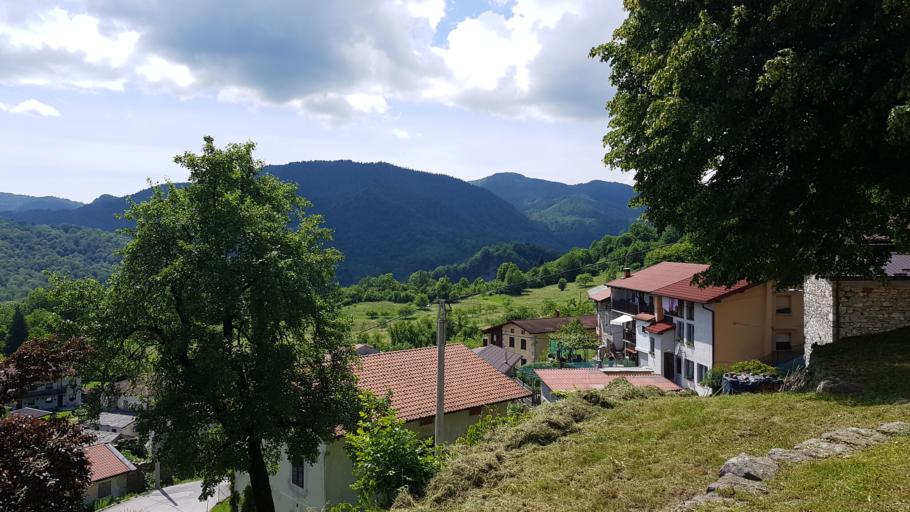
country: IT
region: Friuli Venezia Giulia
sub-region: Provincia di Udine
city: Pulfero
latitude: 46.2337
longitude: 13.4335
